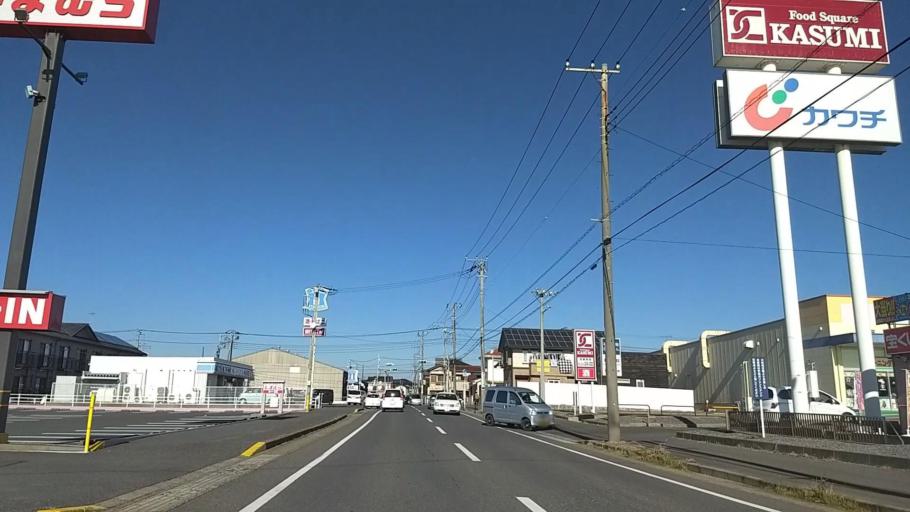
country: JP
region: Chiba
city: Hasaki
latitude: 35.7202
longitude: 140.8357
